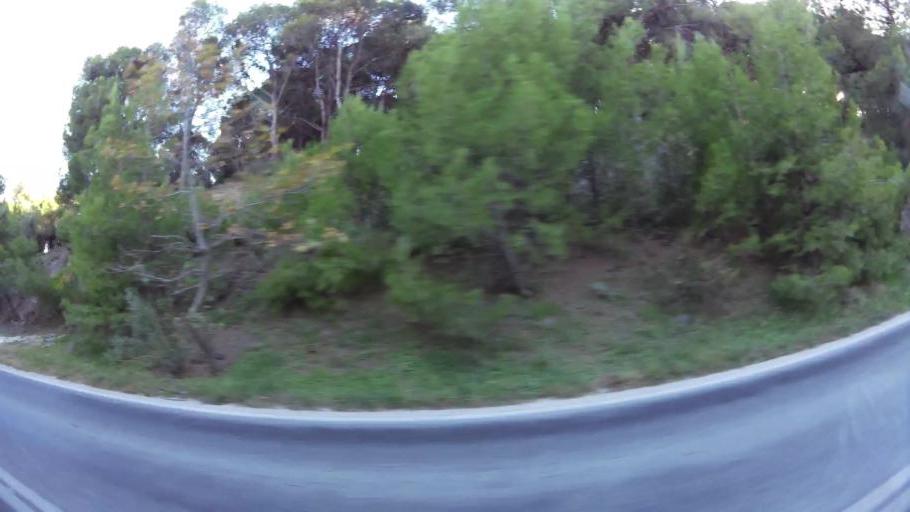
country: GR
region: Attica
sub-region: Nomarchia Athinas
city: Nea Penteli
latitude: 38.0524
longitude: 23.8497
